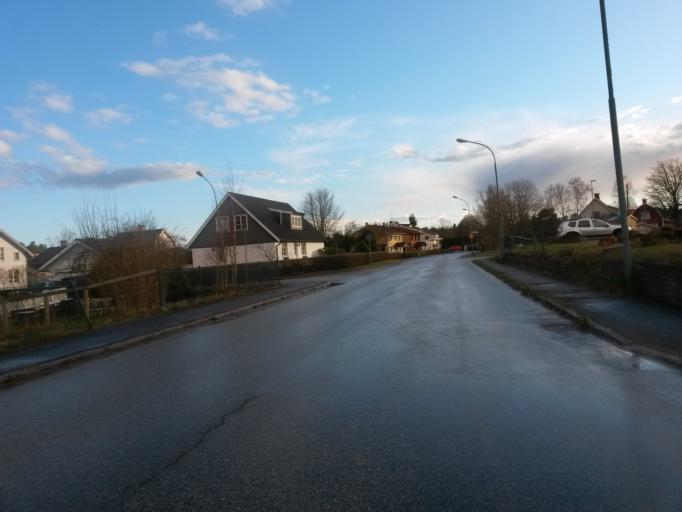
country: SE
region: OErebro
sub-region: Karlskoga Kommun
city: Karlskoga
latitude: 59.3126
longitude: 14.5015
